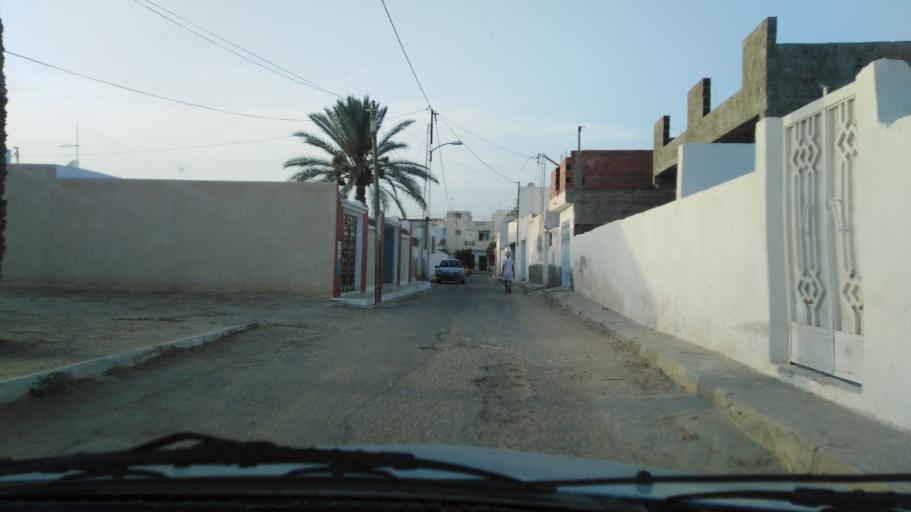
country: TN
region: Qabis
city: Gabes
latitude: 33.9586
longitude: 9.9985
